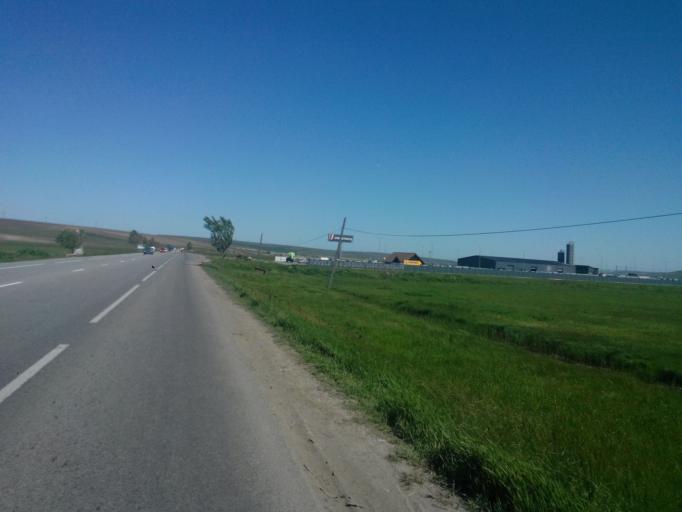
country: RO
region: Iasi
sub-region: Comuna Podu Iloaiei
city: Podu Iloaiei
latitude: 47.2161
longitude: 27.2927
